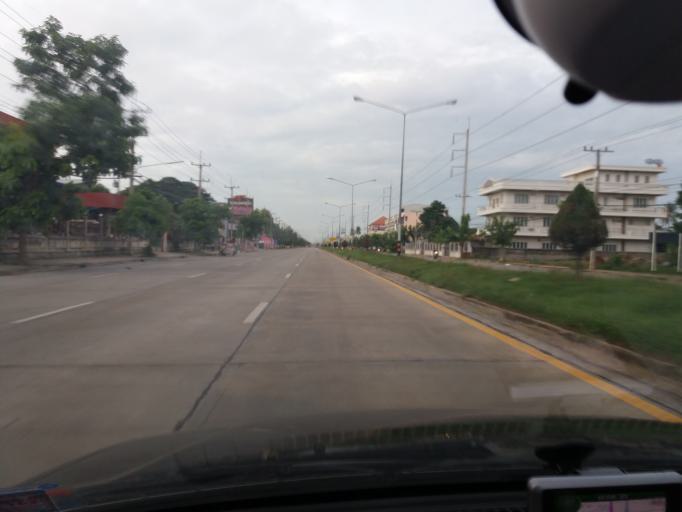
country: TH
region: Suphan Buri
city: U Thong
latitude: 14.3924
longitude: 99.8955
